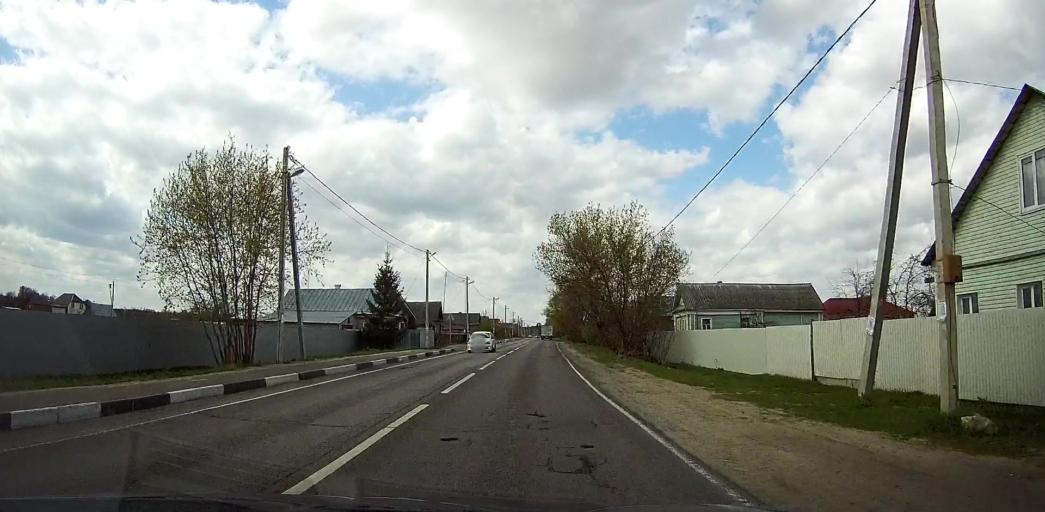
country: RU
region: Moskovskaya
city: Davydovo
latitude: 55.6372
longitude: 38.8672
